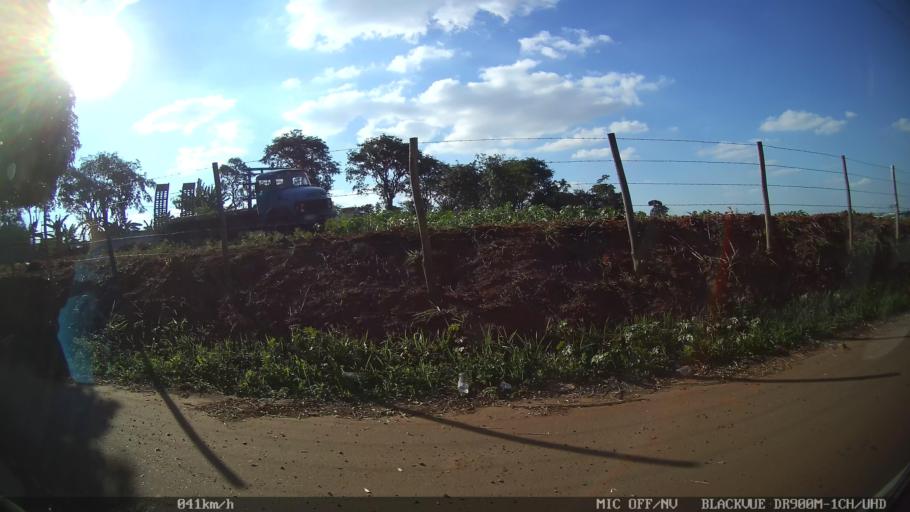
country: BR
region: Sao Paulo
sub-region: Americana
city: Americana
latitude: -22.7847
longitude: -47.3506
